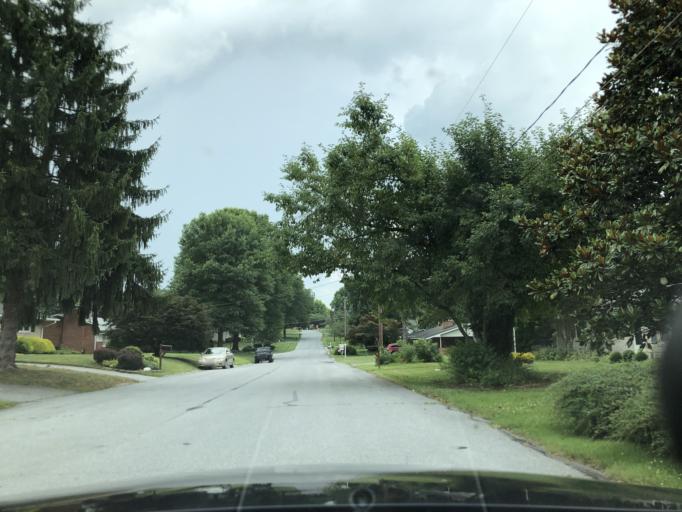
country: US
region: Maryland
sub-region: Carroll County
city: Westminster
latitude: 39.5523
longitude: -76.9848
